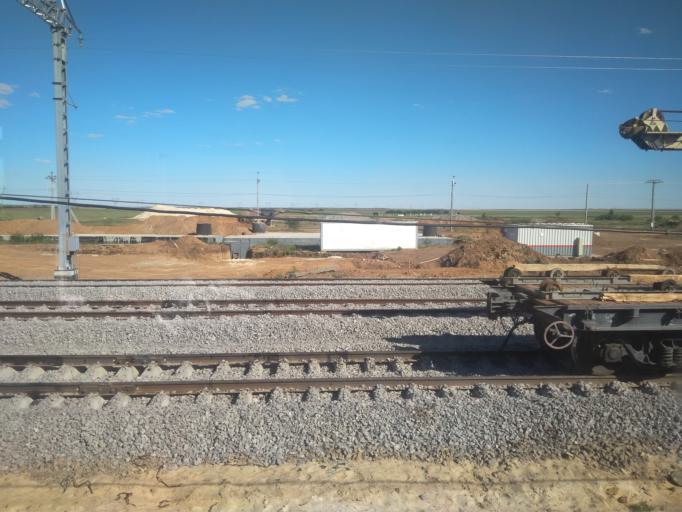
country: RU
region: Volgograd
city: Bereslavka
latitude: 48.2891
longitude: 44.2756
